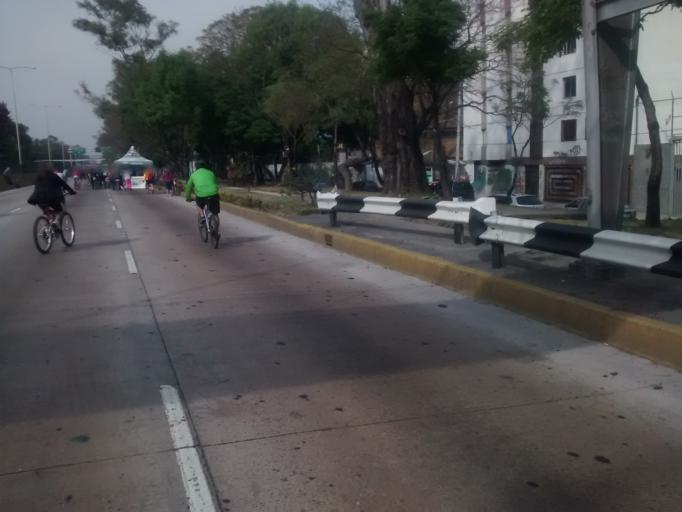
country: MX
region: Mexico City
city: Colonia Nativitas
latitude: 19.3699
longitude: -99.1131
